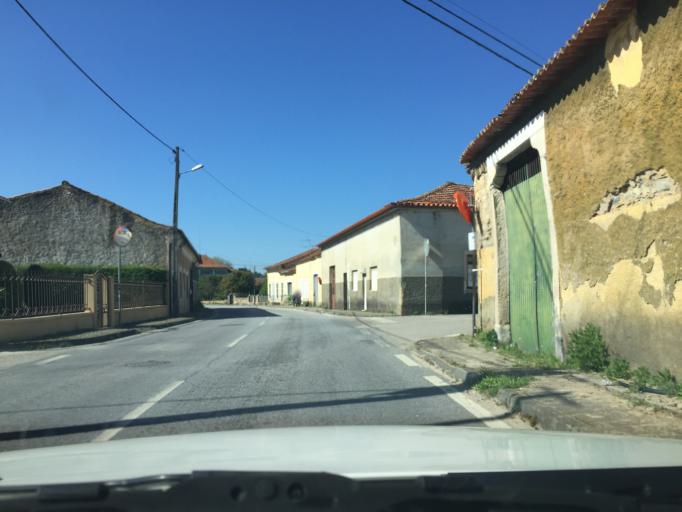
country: PT
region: Aveiro
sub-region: Anadia
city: Sangalhos
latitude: 40.4334
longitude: -8.5100
